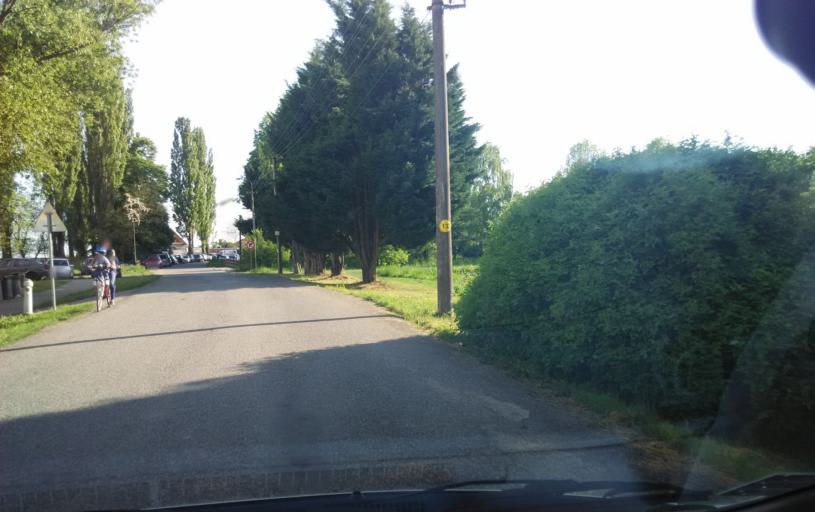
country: SK
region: Nitriansky
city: Levice
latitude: 48.2396
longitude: 18.5702
